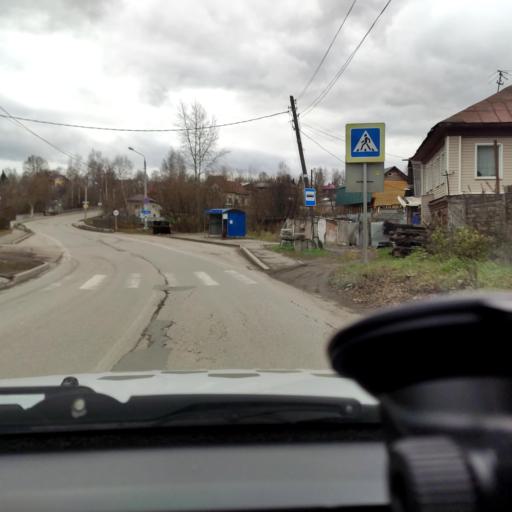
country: RU
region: Perm
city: Perm
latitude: 58.0288
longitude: 56.3140
